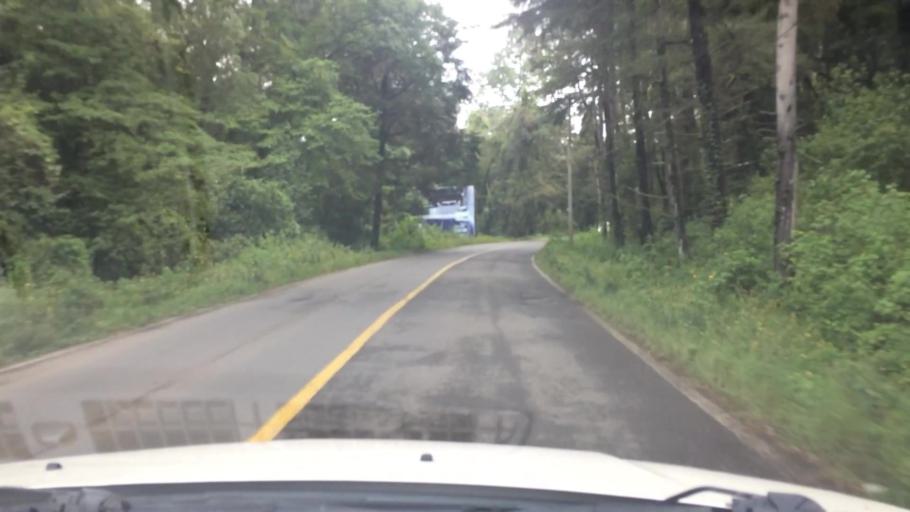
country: MX
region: Mexico
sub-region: Valle de Bravo
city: Cuadrilla de Dolores
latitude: 19.1472
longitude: -100.0614
